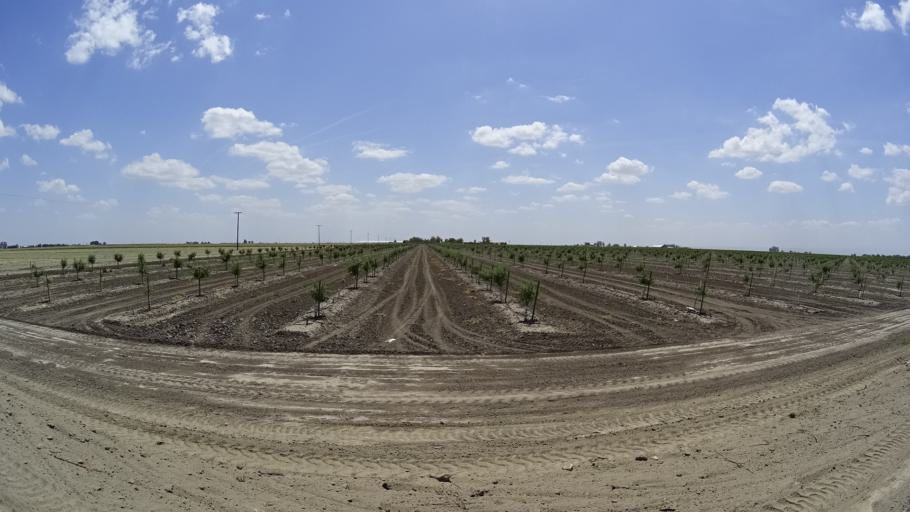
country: US
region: California
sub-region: Kings County
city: Stratford
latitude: 36.1823
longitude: -119.7989
